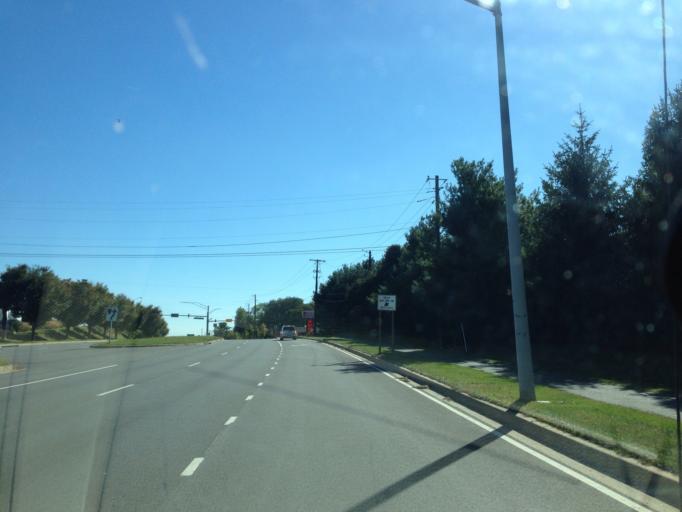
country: US
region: Maryland
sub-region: Montgomery County
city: Germantown
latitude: 39.1969
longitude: -77.2448
